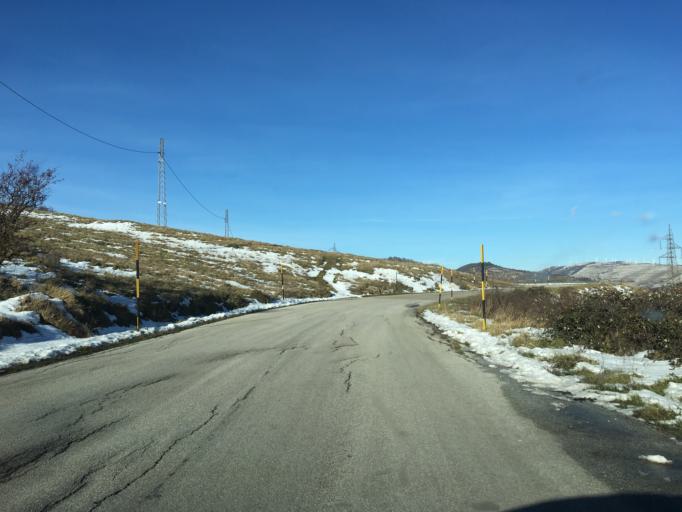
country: IT
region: Abruzzo
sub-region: Provincia di Chieti
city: Rosello
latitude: 41.8582
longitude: 14.3563
